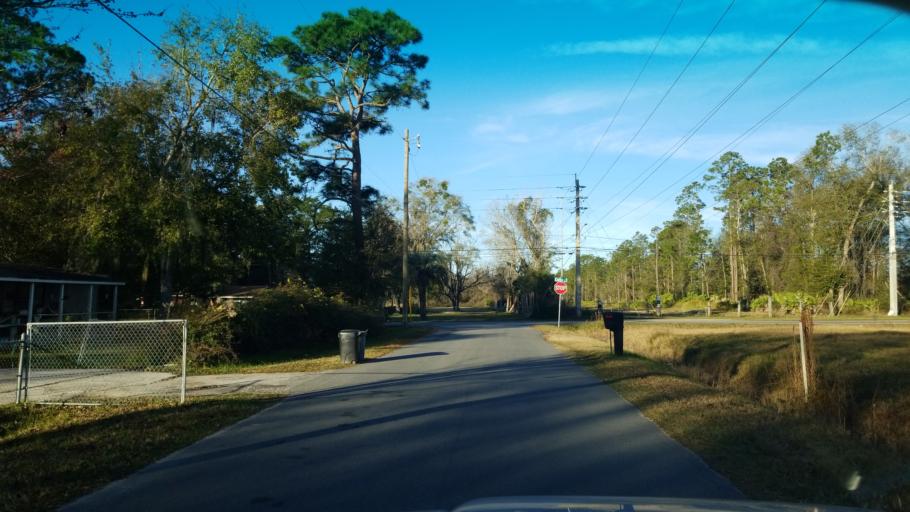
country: US
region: Florida
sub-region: Duval County
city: Baldwin
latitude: 30.3235
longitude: -81.8479
